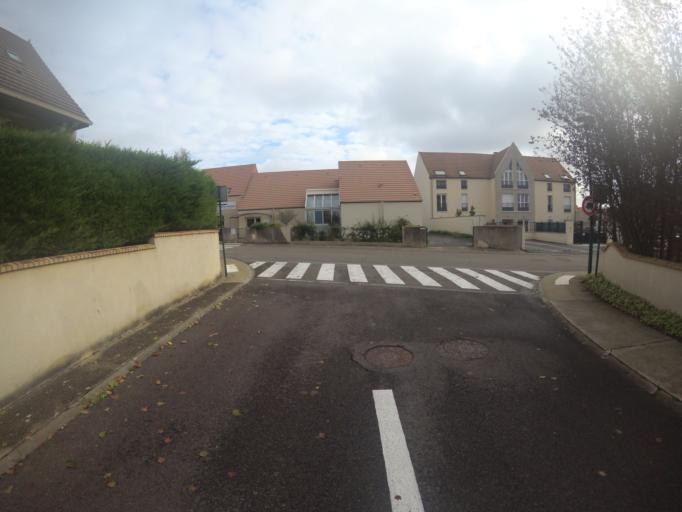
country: FR
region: Ile-de-France
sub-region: Departement de Seine-et-Marne
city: Montevrain
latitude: 48.8747
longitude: 2.7525
